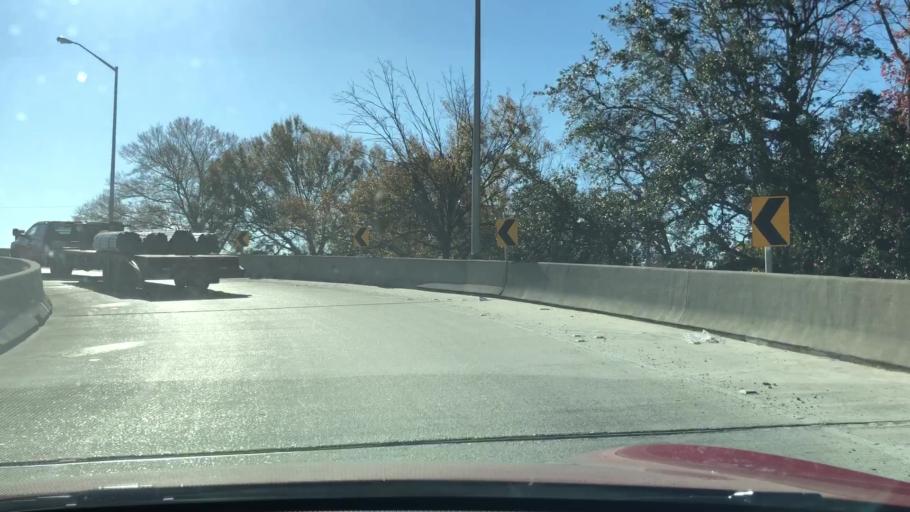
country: US
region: Louisiana
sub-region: Jefferson Parish
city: Jefferson
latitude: 29.9625
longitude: -90.1578
